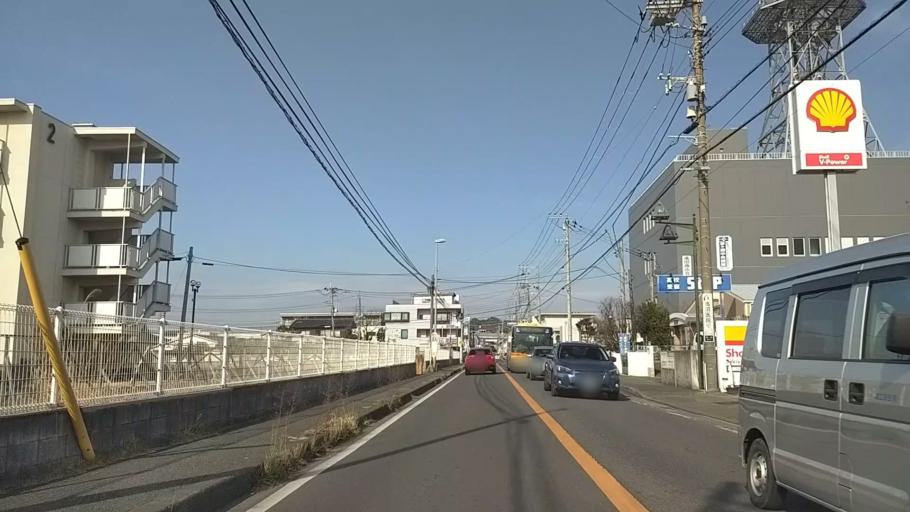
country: JP
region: Kanagawa
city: Chigasaki
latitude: 35.3460
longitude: 139.4130
